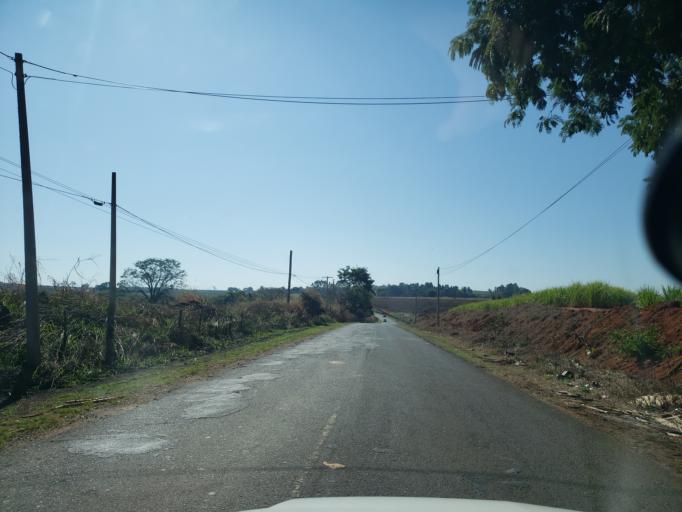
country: BR
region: Sao Paulo
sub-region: Moji-Guacu
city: Mogi-Gaucu
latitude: -22.3529
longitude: -46.8997
